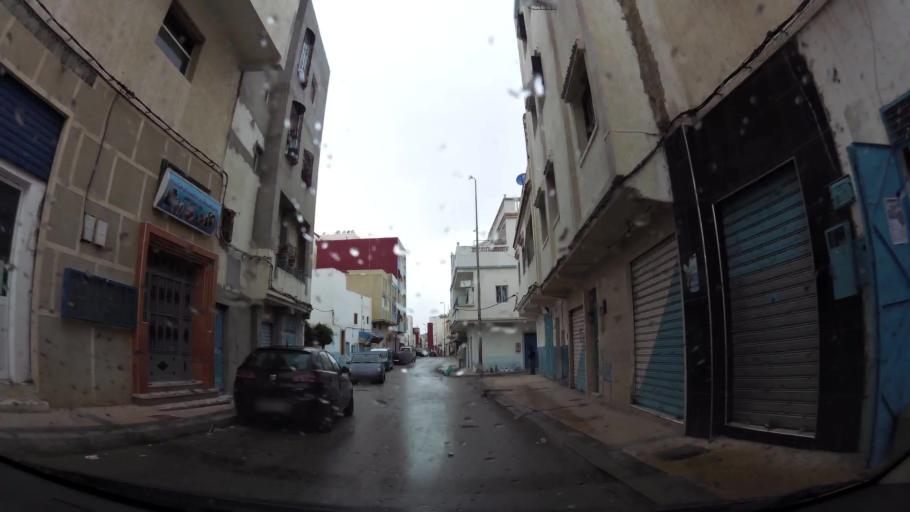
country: MA
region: Tanger-Tetouan
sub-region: Tetouan
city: Martil
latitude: 35.6210
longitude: -5.2777
